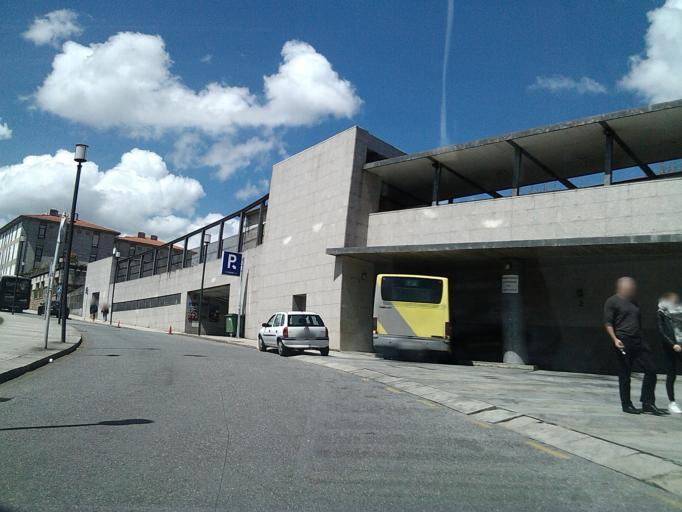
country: ES
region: Galicia
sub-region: Provincia da Coruna
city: Santiago de Compostela
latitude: 42.8832
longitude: -8.5402
